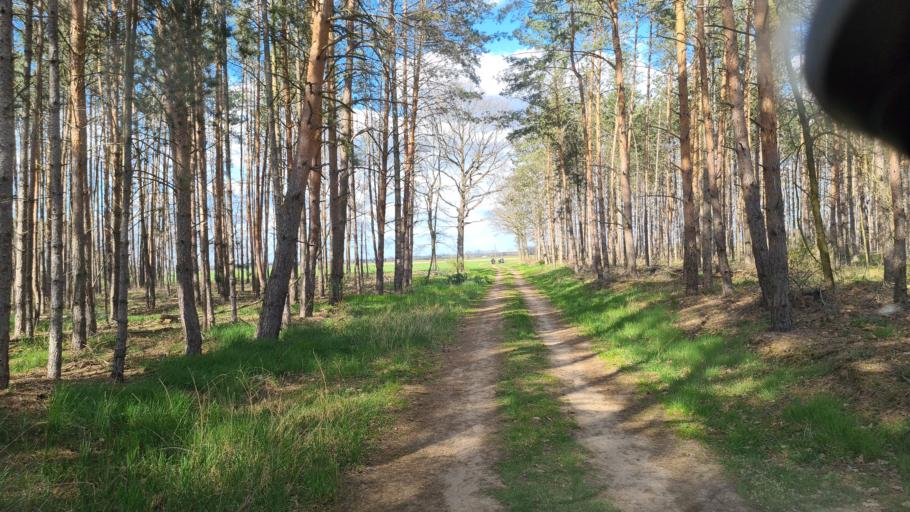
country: DE
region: Brandenburg
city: Falkenberg
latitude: 51.5284
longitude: 13.2857
